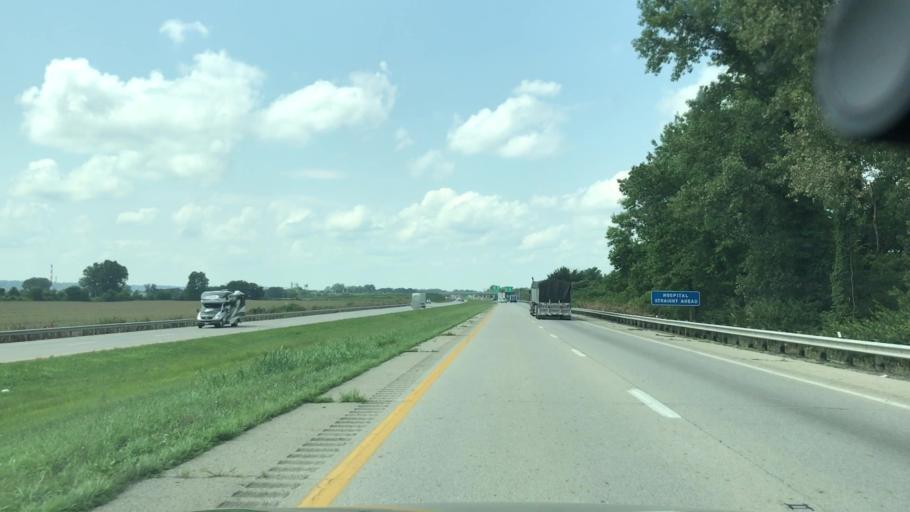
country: US
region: Ohio
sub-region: Ross County
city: Chillicothe
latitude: 39.3103
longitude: -82.9248
